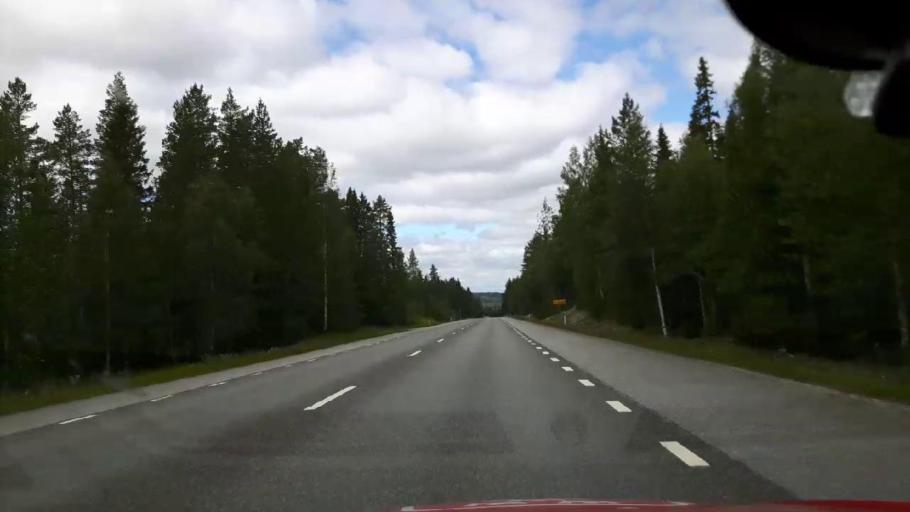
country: SE
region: Jaemtland
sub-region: Braecke Kommun
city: Braecke
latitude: 62.7118
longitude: 15.4736
